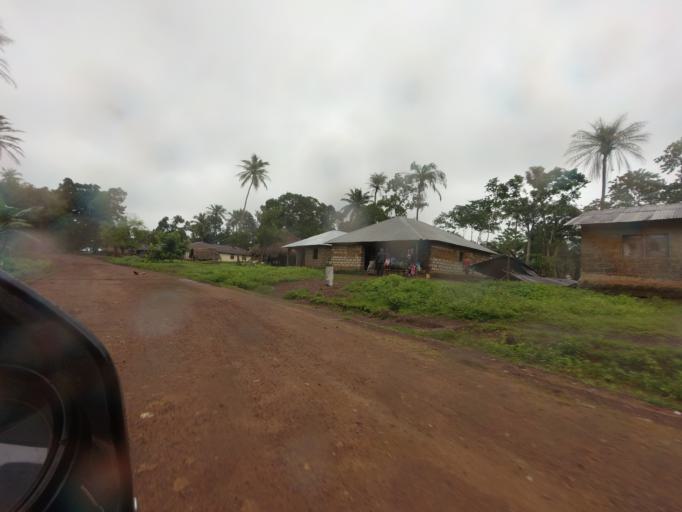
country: SL
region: Northern Province
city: Kambia
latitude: 9.1391
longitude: -12.8800
